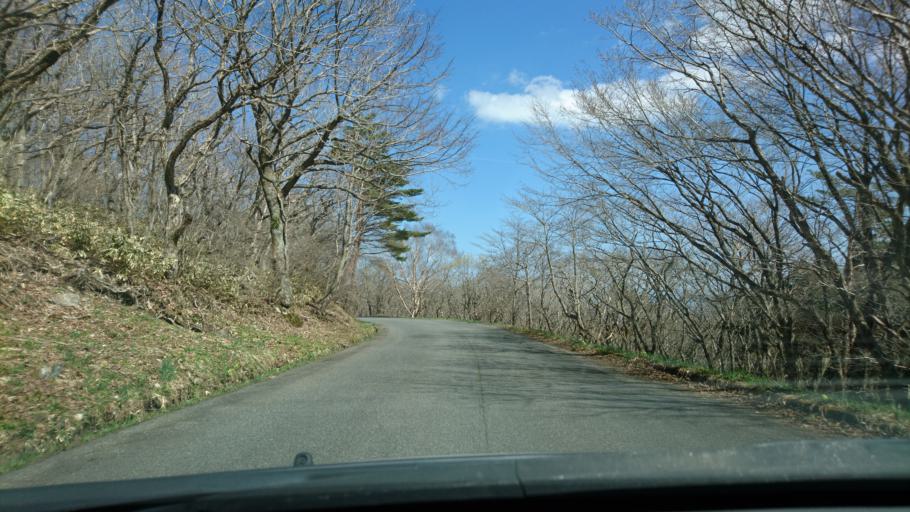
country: JP
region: Iwate
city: Ofunato
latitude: 38.9727
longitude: 141.4504
